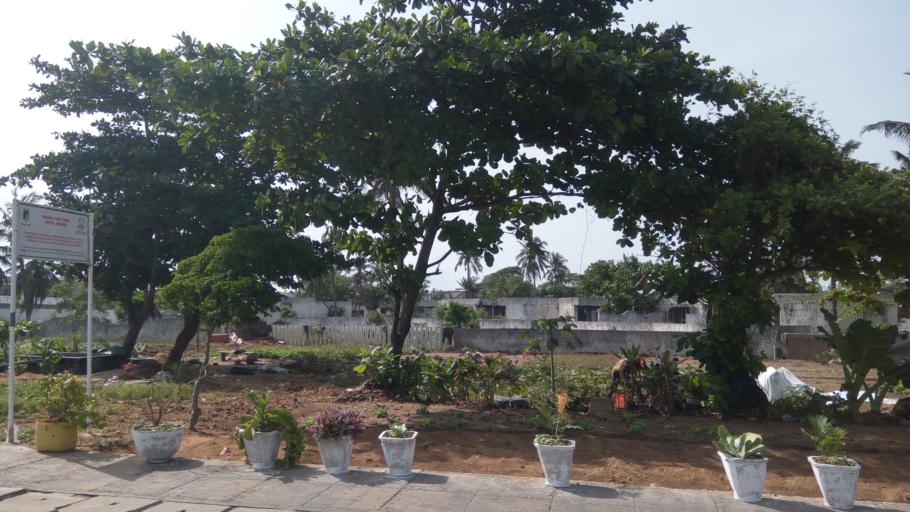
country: TG
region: Maritime
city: Lome
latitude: 6.1306
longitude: 1.2456
